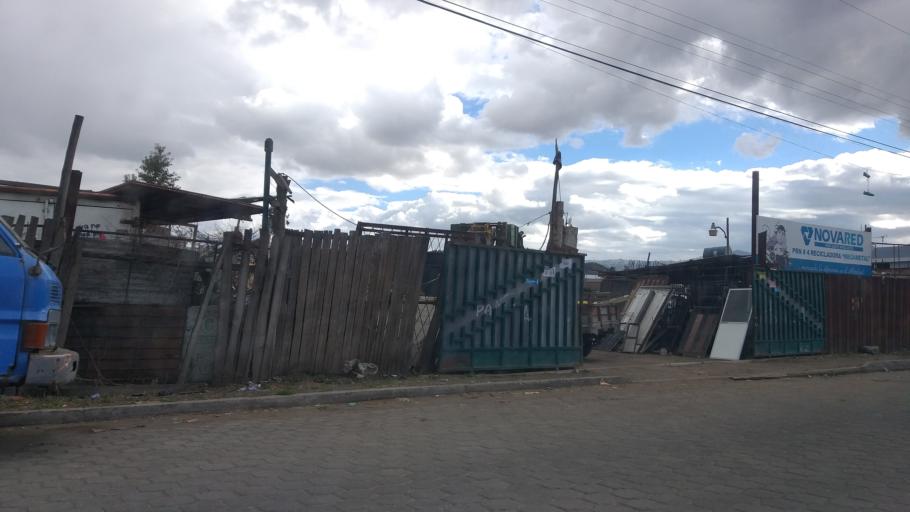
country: EC
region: Chimborazo
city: Riobamba
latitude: -1.6871
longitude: -78.6290
